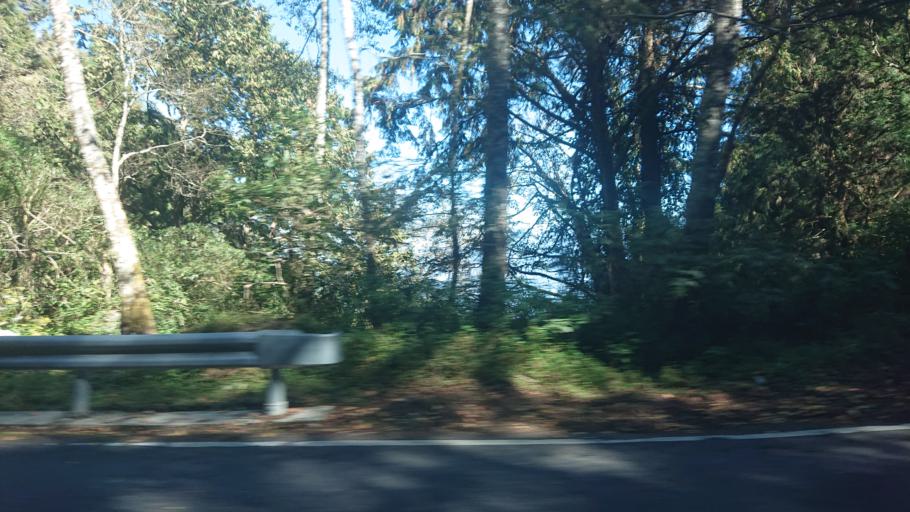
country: TW
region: Taiwan
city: Lugu
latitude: 23.4772
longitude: 120.8348
